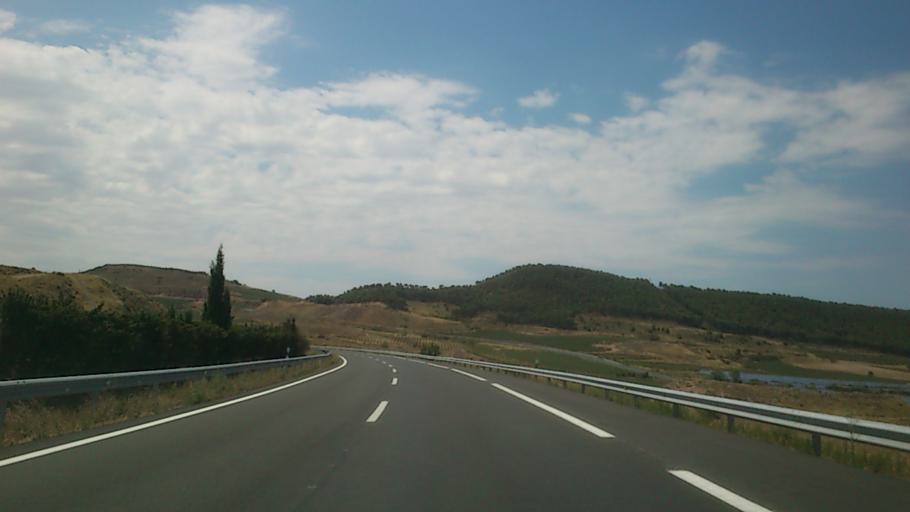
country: ES
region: La Rioja
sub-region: Provincia de La Rioja
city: Cenicero
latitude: 42.4646
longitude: -2.6067
